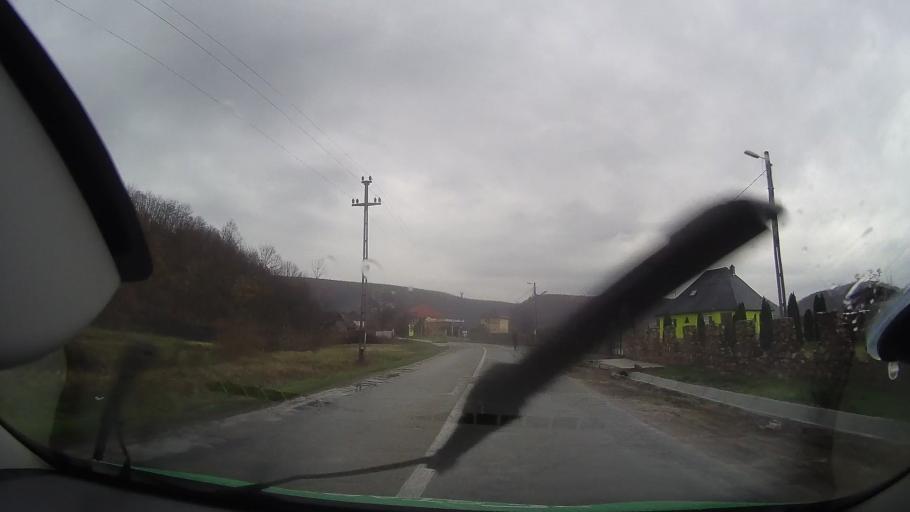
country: RO
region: Bihor
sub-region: Comuna Soimi
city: Soimi
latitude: 46.6842
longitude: 22.1115
